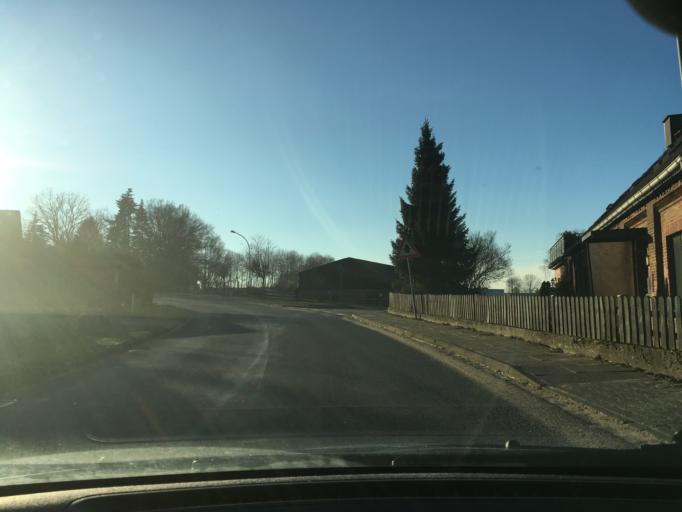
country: DE
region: Schleswig-Holstein
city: Mussen
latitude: 53.4956
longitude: 10.5580
